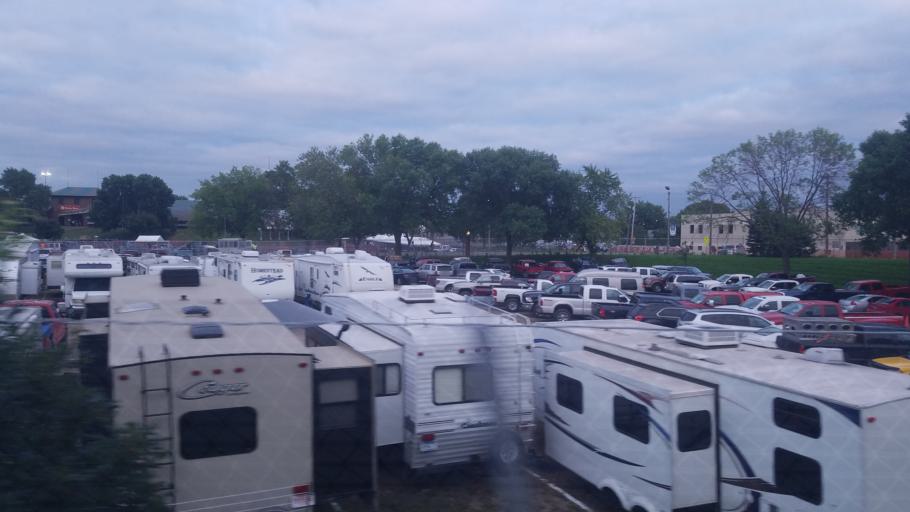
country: US
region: Minnesota
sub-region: Ramsey County
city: Falcon Heights
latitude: 44.9772
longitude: -93.1810
